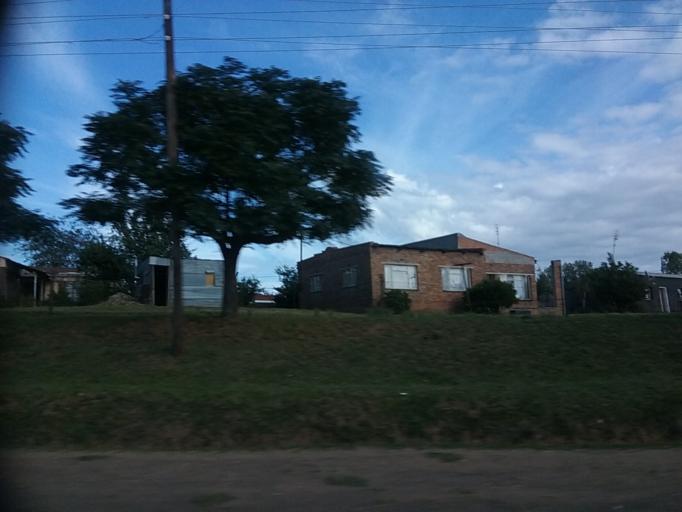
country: LS
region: Berea
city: Teyateyaneng
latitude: -29.1425
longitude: 27.7513
